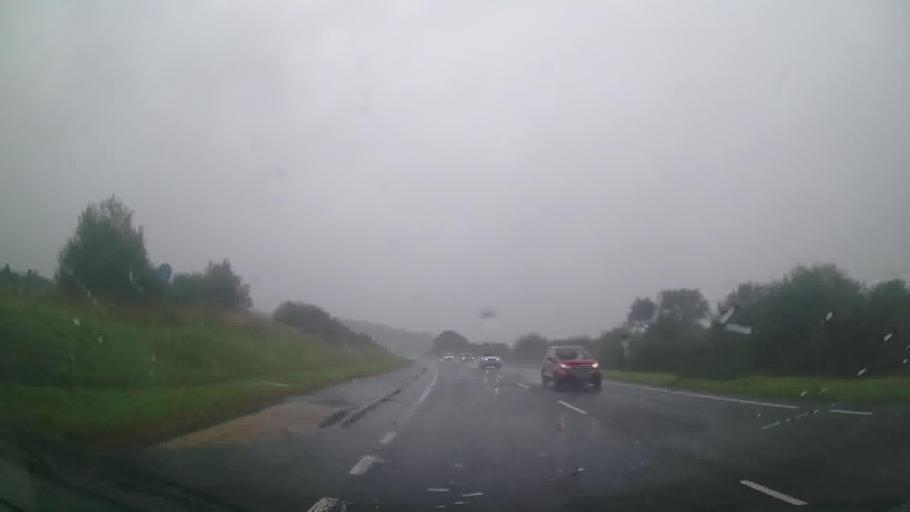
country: GB
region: Wales
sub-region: Carmarthenshire
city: Llanddowror
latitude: 51.8093
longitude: -4.5194
